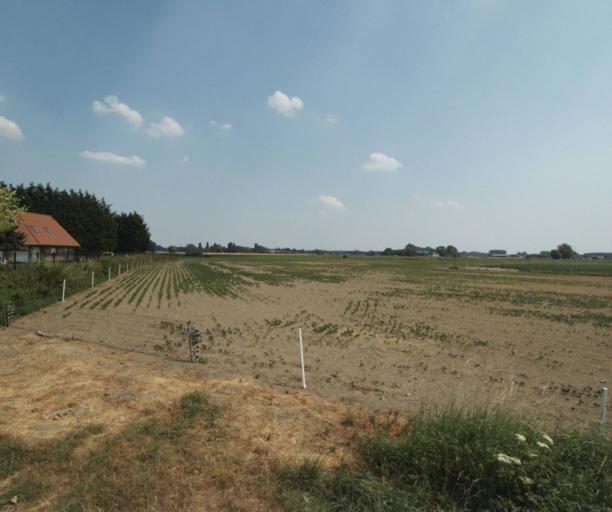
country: FR
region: Nord-Pas-de-Calais
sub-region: Departement du Nord
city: Wambrechies
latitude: 50.7221
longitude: 3.0401
